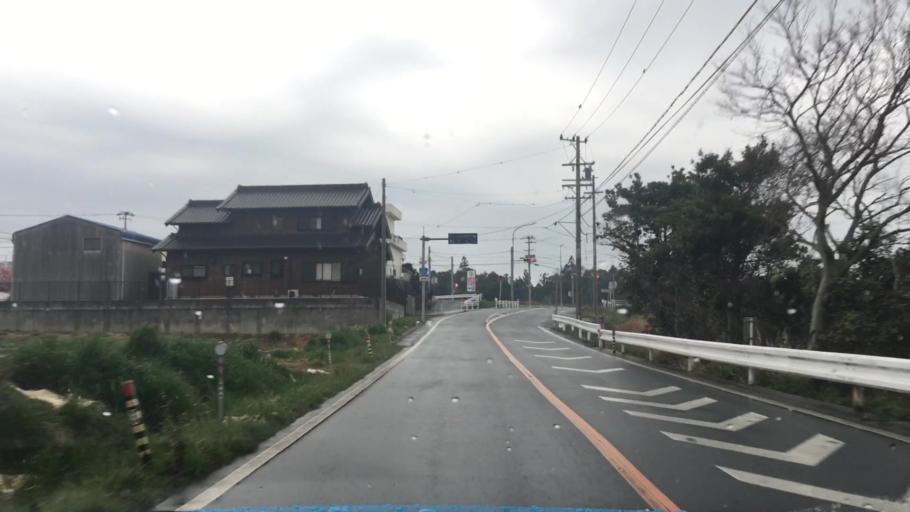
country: JP
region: Aichi
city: Toyohashi
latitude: 34.6672
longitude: 137.3886
